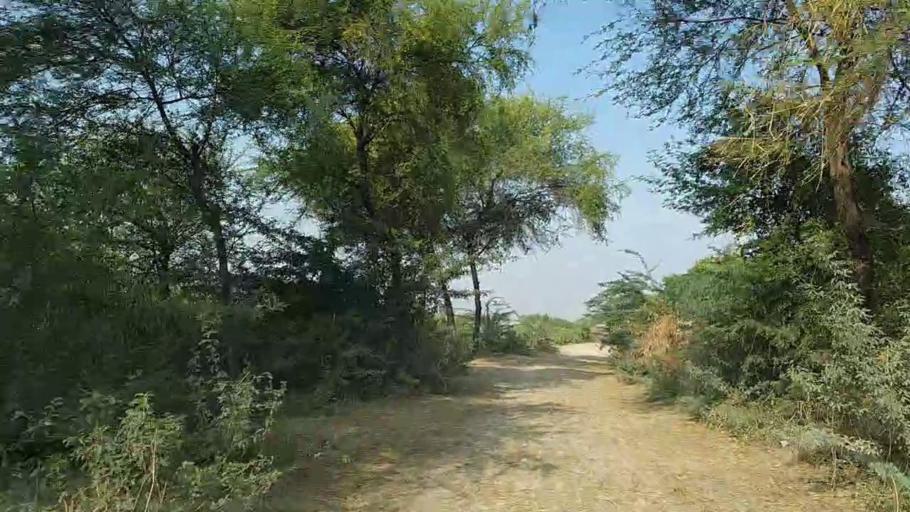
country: PK
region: Sindh
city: Mirpur Batoro
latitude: 24.7180
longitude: 68.2209
